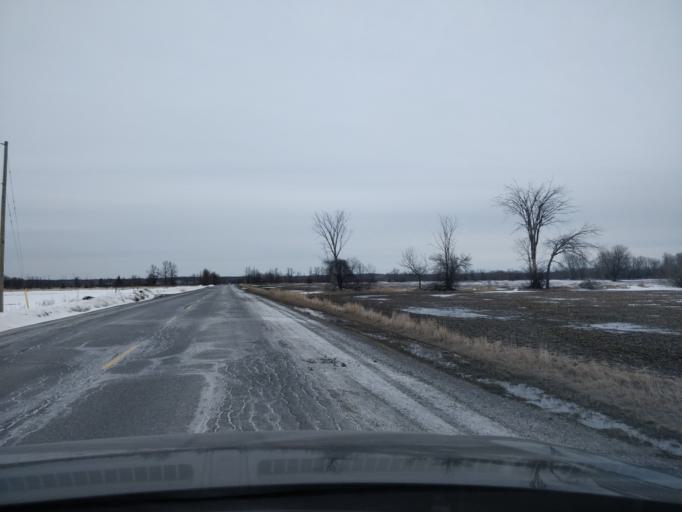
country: CA
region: Ontario
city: Bells Corners
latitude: 45.2582
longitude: -75.8695
